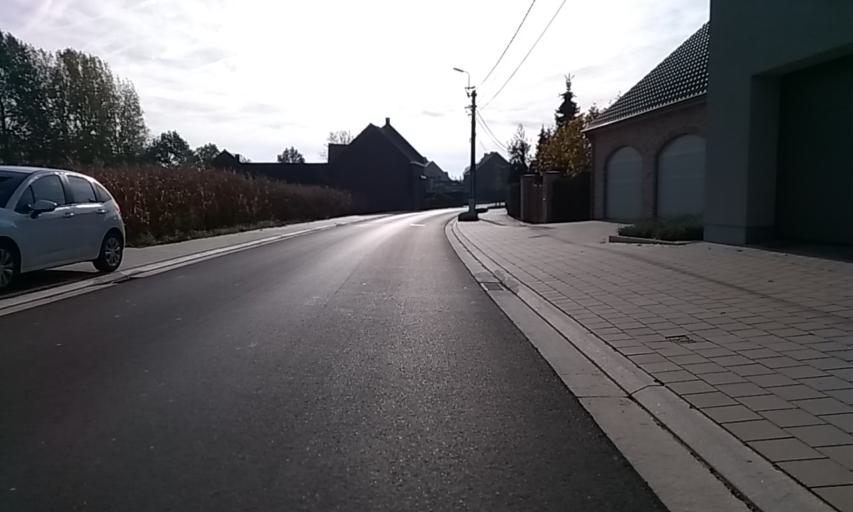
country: BE
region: Flanders
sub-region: Provincie Oost-Vlaanderen
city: Sint-Lievens-Houtem
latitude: 50.9277
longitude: 3.8930
